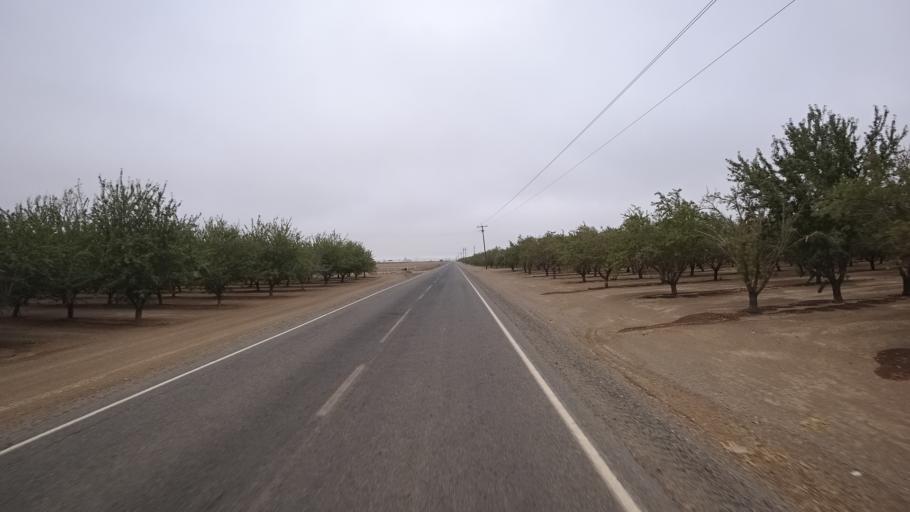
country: US
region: California
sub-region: Yolo County
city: Dunnigan
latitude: 38.9255
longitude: -121.9785
